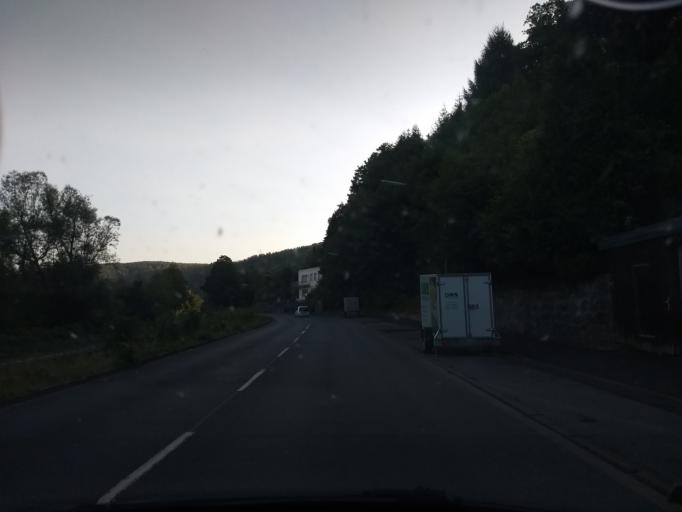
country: DE
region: North Rhine-Westphalia
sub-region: Regierungsbezirk Arnsberg
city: Arnsberg
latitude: 51.3977
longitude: 8.0562
